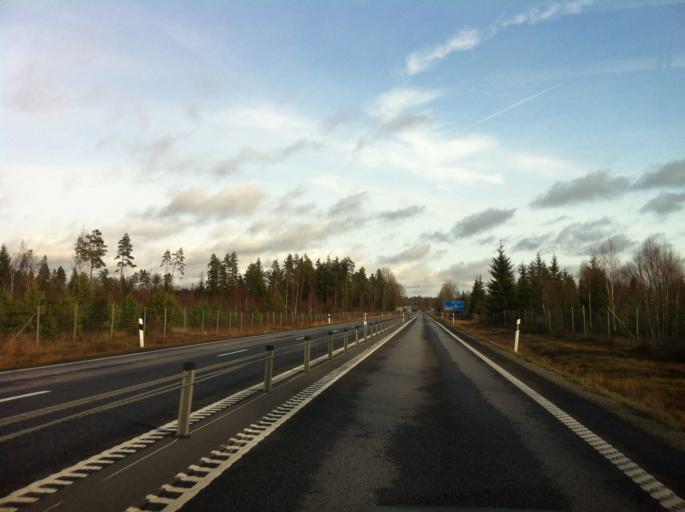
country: SE
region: Kronoberg
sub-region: Almhults Kommun
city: AElmhult
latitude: 56.6585
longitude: 14.2894
